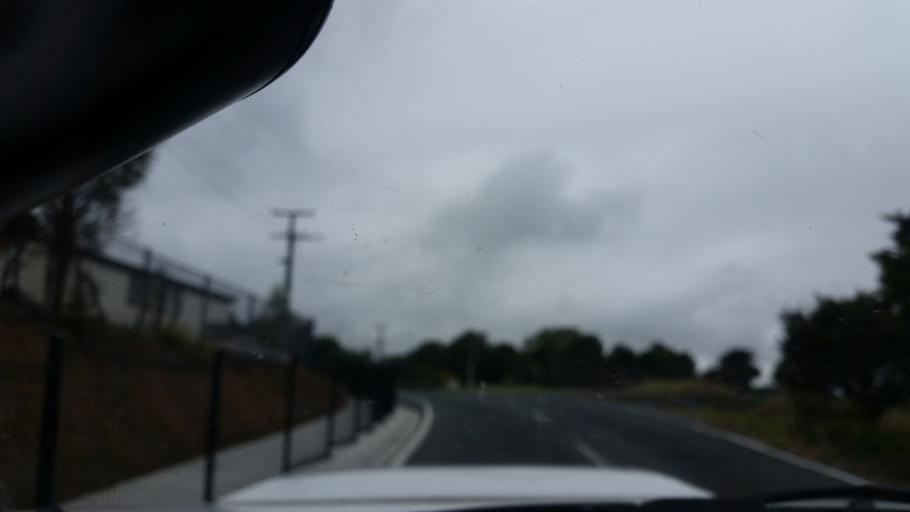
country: NZ
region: Auckland
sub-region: Auckland
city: Wellsford
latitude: -36.1601
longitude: 174.4468
